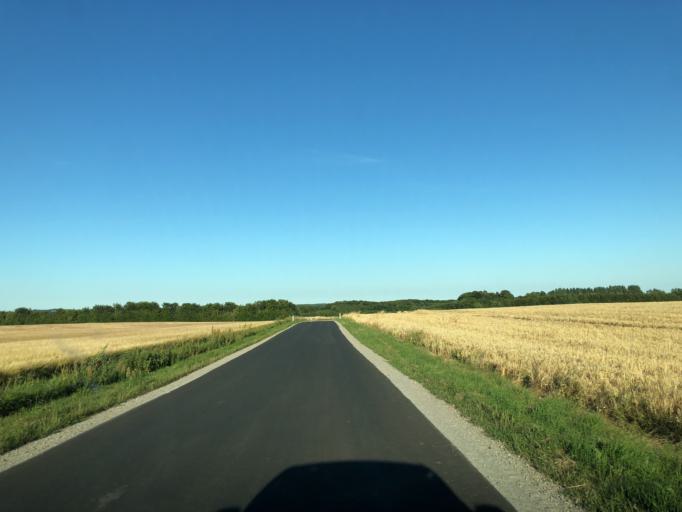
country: DK
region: Central Jutland
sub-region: Horsens Kommune
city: Horsens
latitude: 55.9610
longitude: 9.8293
